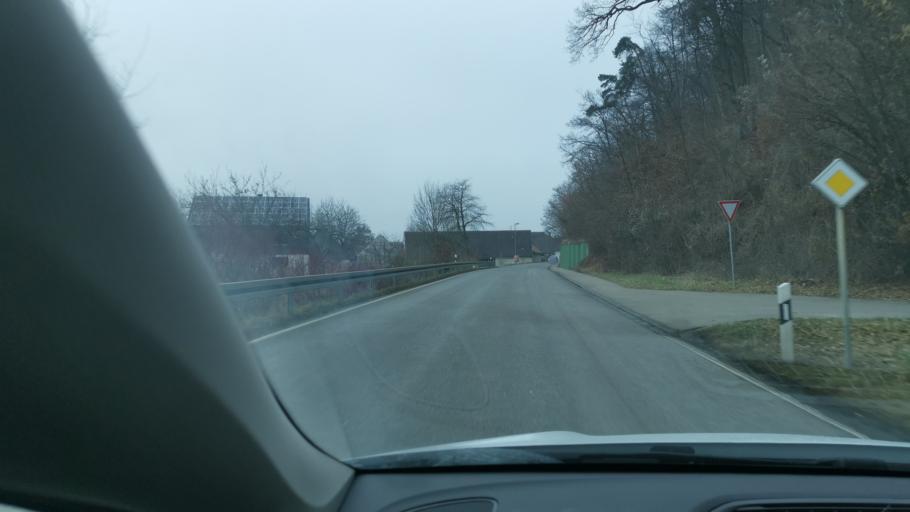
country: DE
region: Bavaria
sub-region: Swabia
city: Rehling
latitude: 48.4912
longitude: 10.9219
